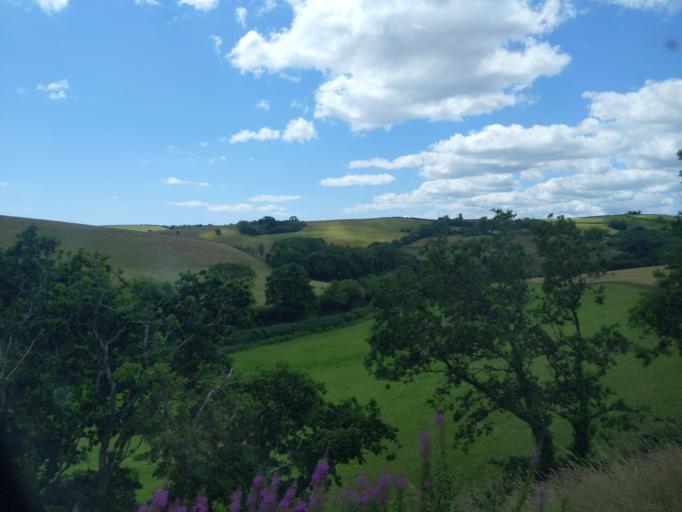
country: GB
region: England
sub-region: Cornwall
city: Pillaton
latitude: 50.3986
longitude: -4.3406
